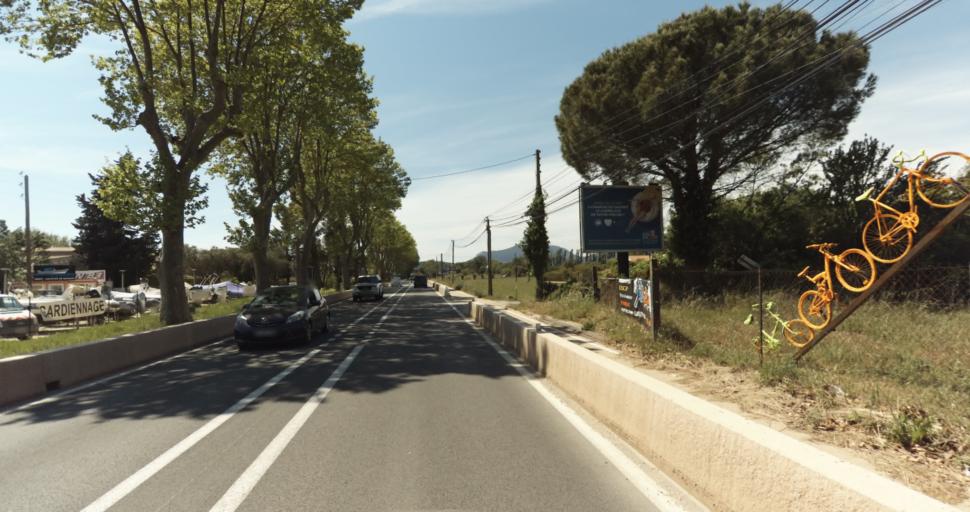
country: FR
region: Provence-Alpes-Cote d'Azur
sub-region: Departement du Var
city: La Crau
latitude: 43.1315
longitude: 6.0530
